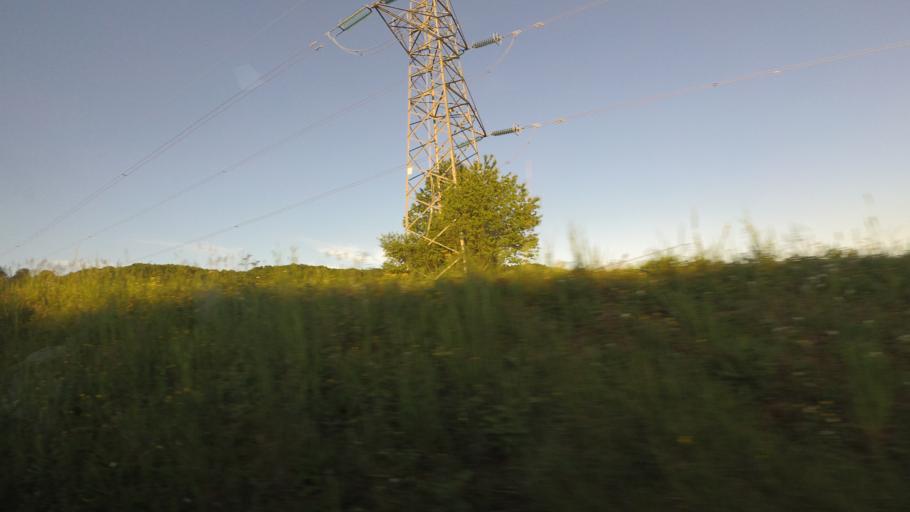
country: HR
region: Karlovacka
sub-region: Grad Karlovac
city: Karlovac
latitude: 45.4222
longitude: 15.5496
